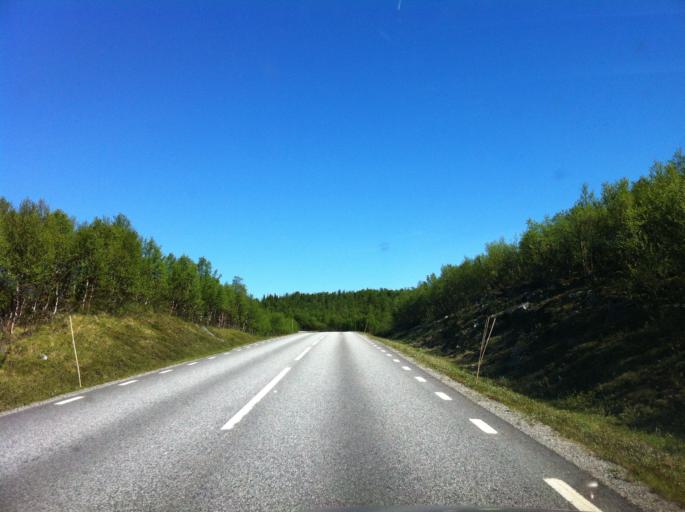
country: NO
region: Sor-Trondelag
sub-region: Tydal
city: Aas
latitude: 62.6050
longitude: 12.1660
